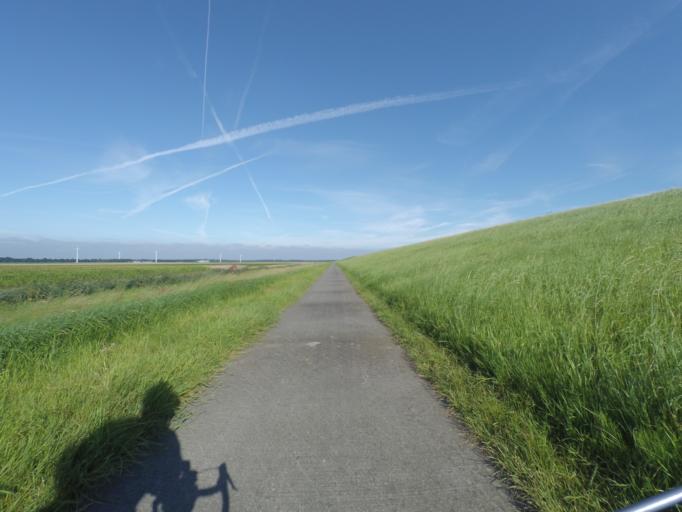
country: NL
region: Flevoland
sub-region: Gemeente Lelystad
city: Lelystad
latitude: 52.4243
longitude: 5.4683
